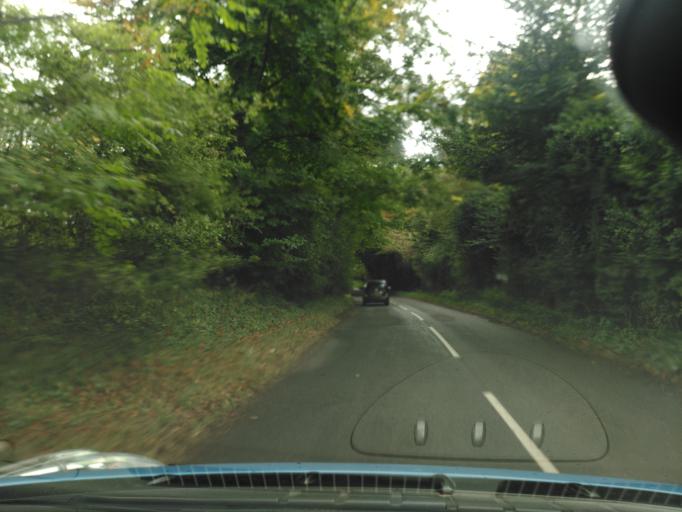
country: GB
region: England
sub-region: Oxfordshire
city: Stanford in the Vale
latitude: 51.5824
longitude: -1.5273
